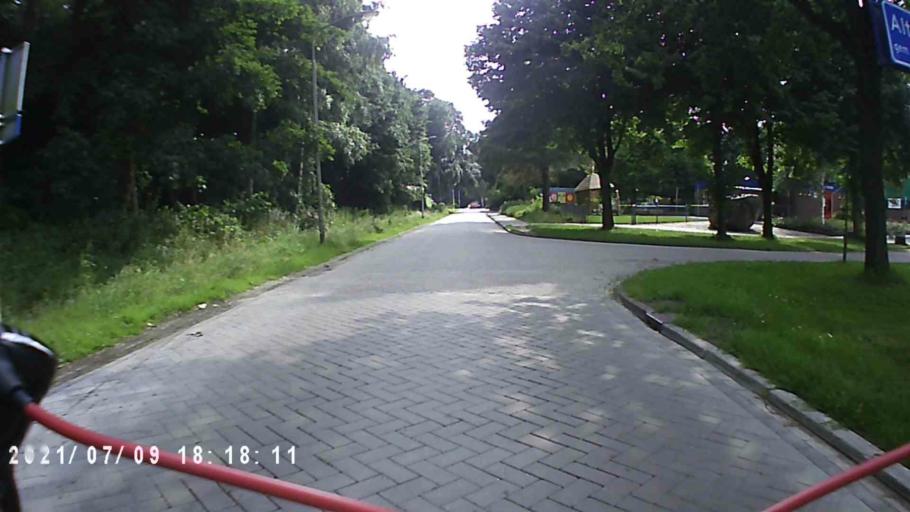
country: NL
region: Groningen
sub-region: Gemeente Pekela
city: Oude Pekela
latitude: 53.0508
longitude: 7.0070
